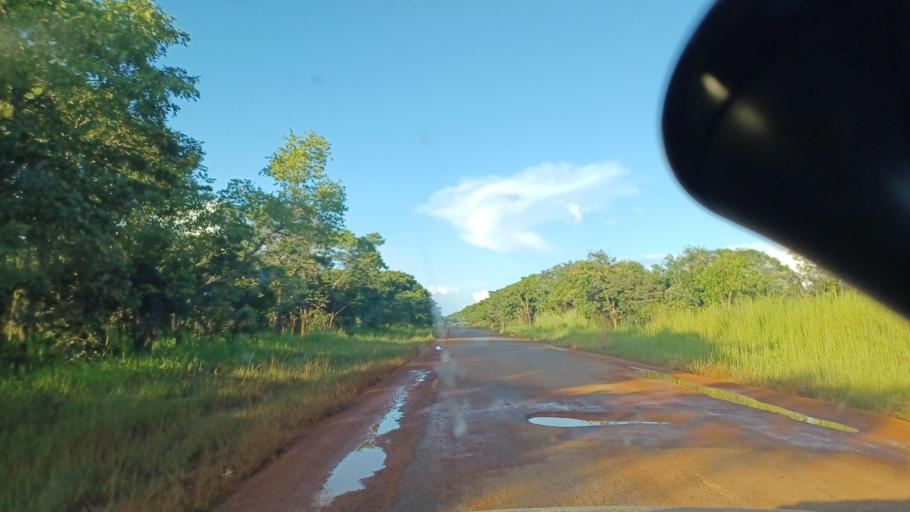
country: ZM
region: North-Western
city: Kalengwa
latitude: -13.1388
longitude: 25.0701
